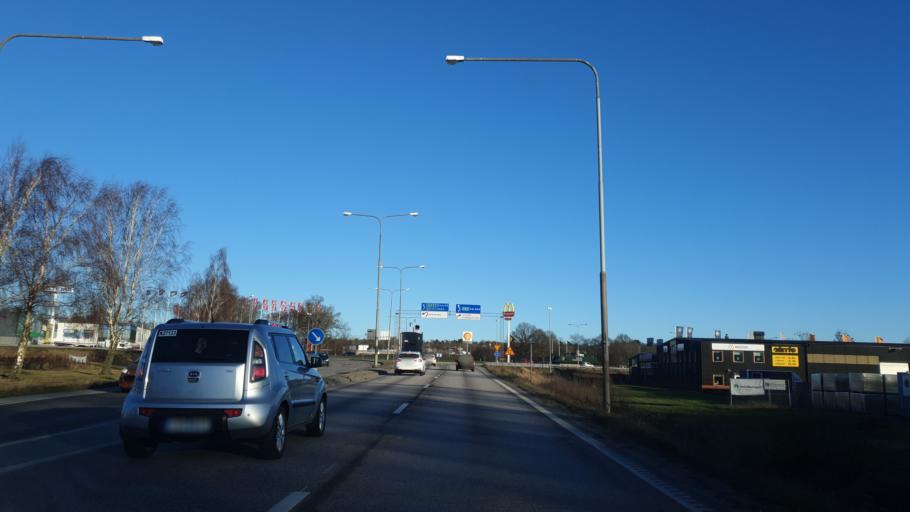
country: SE
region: Blekinge
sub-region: Karlskrona Kommun
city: Rodeby
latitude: 56.2021
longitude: 15.6384
